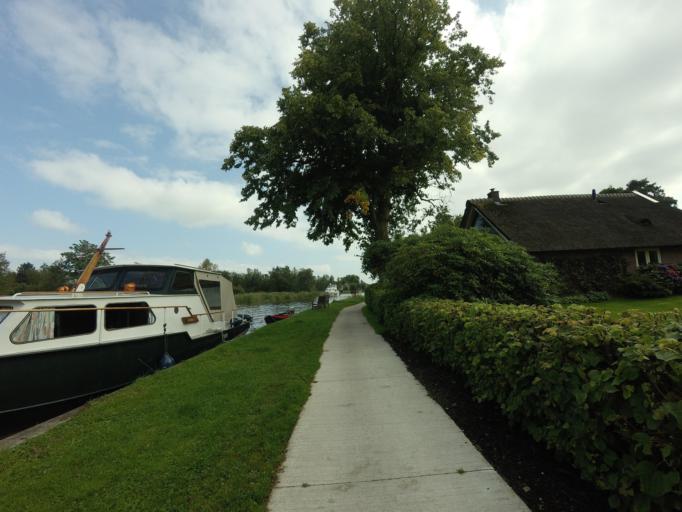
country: NL
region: Overijssel
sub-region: Gemeente Steenwijkerland
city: Oldemarkt
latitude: 52.7967
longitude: 5.9314
